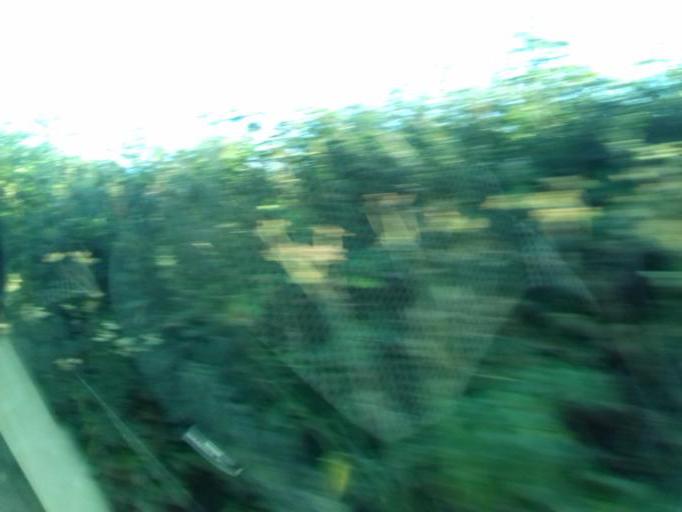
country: IE
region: Leinster
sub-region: Fingal County
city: Swords
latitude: 53.4958
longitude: -6.2838
